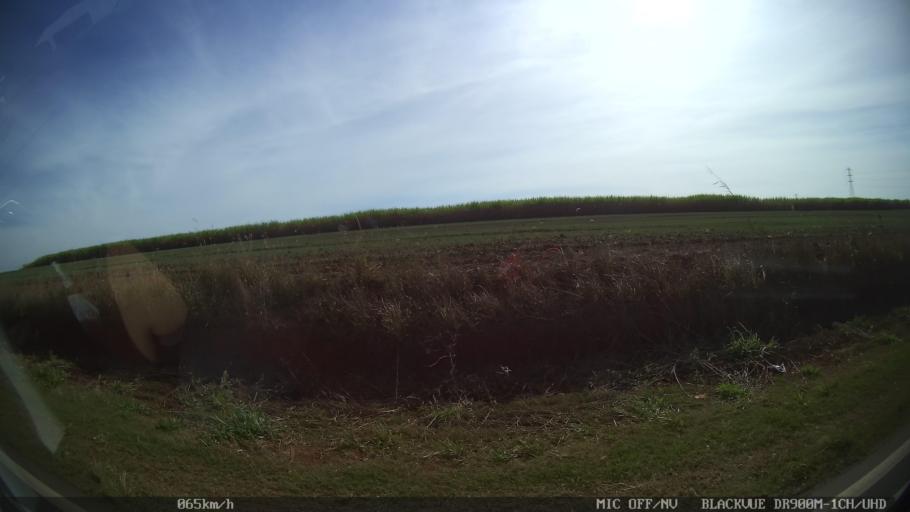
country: BR
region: Sao Paulo
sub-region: Rio Das Pedras
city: Rio das Pedras
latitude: -22.7895
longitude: -47.6399
